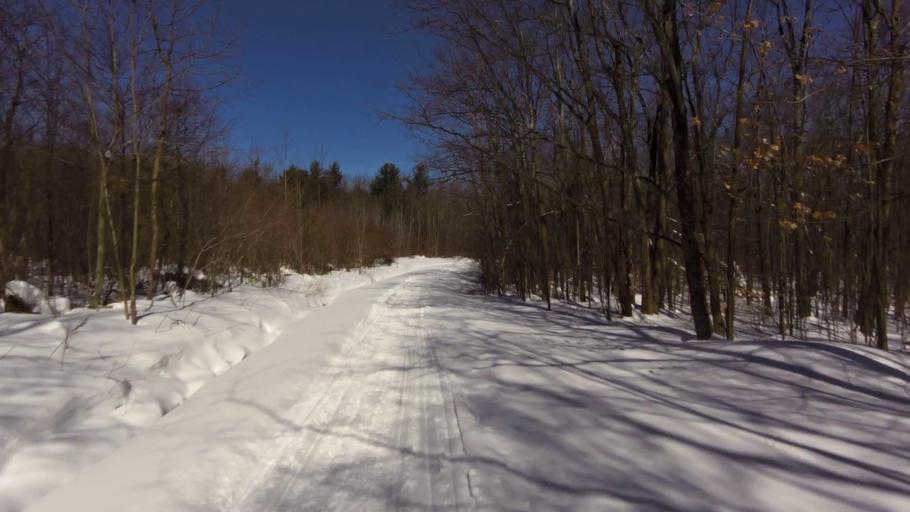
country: US
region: New York
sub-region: Allegany County
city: Cuba
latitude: 42.3227
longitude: -78.2329
